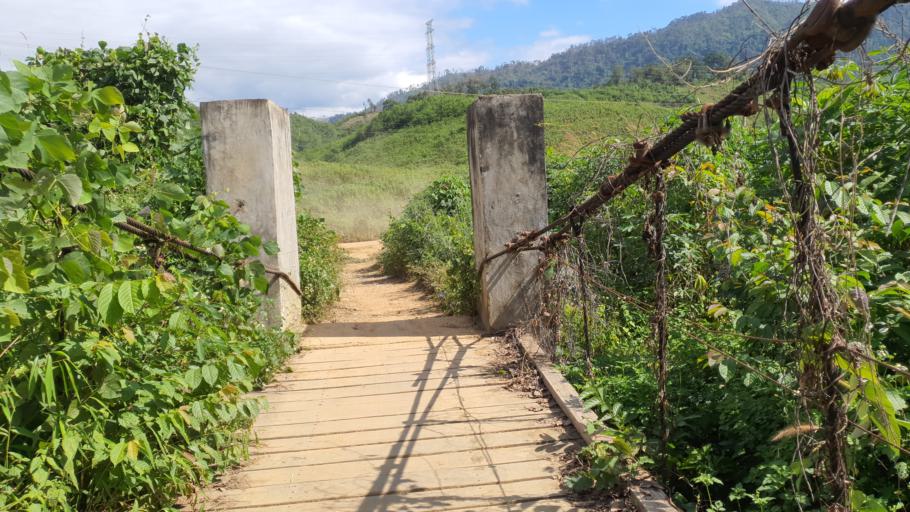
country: LA
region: Bolikhamxai
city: Bolikhan
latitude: 18.9099
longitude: 103.7432
